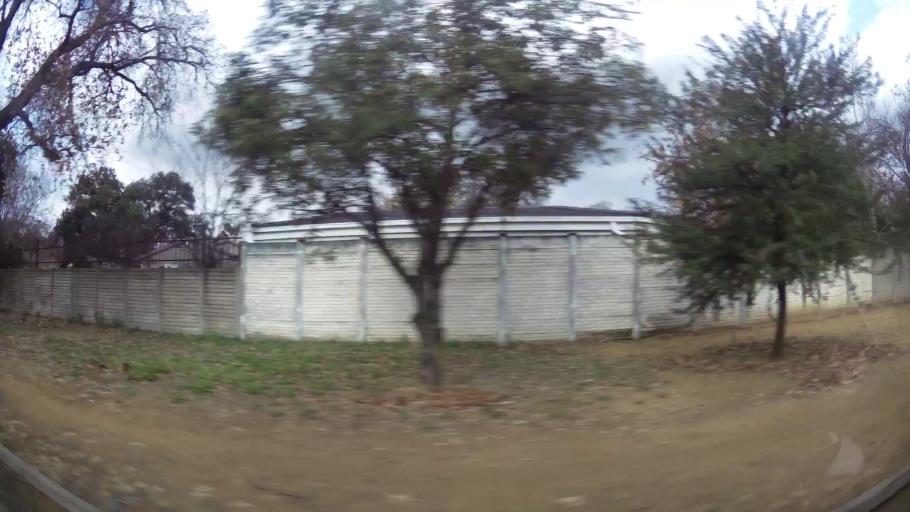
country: ZA
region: Orange Free State
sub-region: Fezile Dabi District Municipality
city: Sasolburg
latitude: -26.8060
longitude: 27.8297
